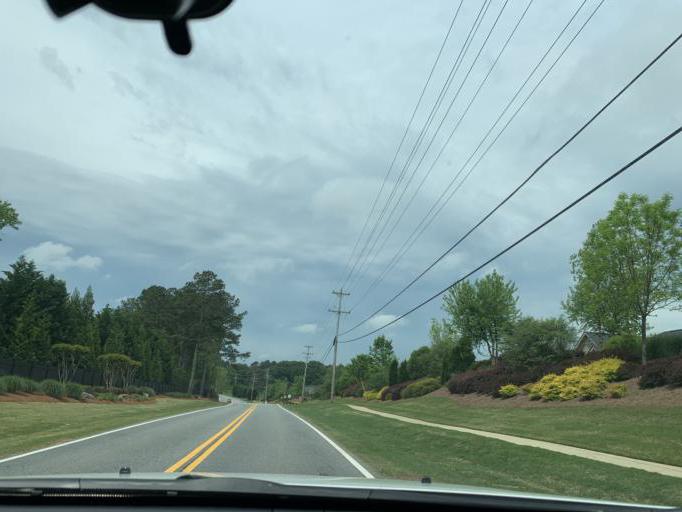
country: US
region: Georgia
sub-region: Forsyth County
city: Cumming
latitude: 34.1361
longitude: -84.1773
